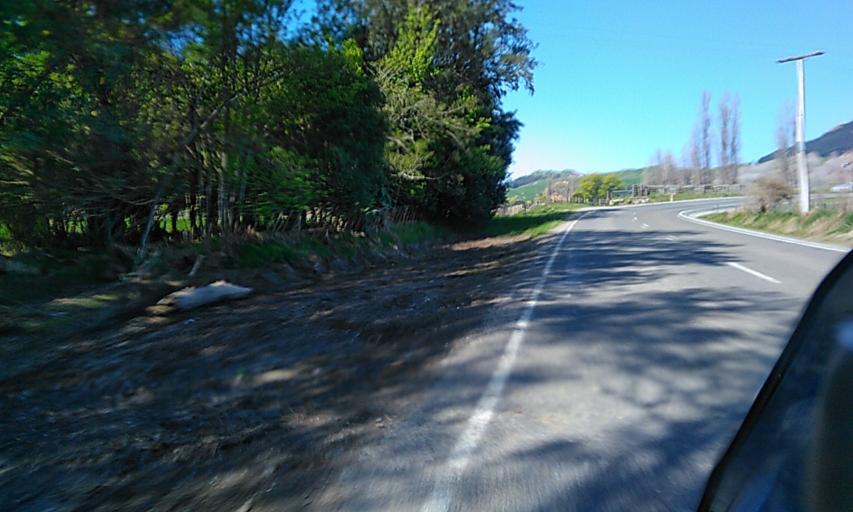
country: NZ
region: Gisborne
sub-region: Gisborne District
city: Gisborne
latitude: -38.3590
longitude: 178.1988
